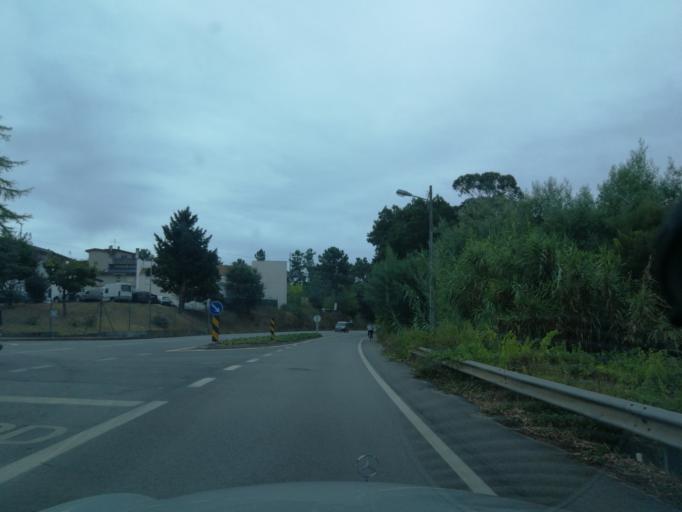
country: PT
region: Aveiro
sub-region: Agueda
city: Agueda
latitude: 40.5854
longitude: -8.4492
